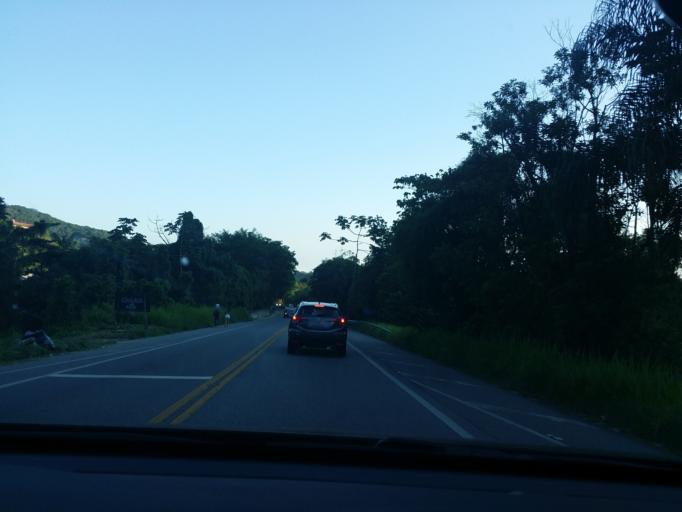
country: BR
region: Sao Paulo
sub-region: Sao Sebastiao
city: Sao Sebastiao
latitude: -23.7546
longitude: -45.7249
